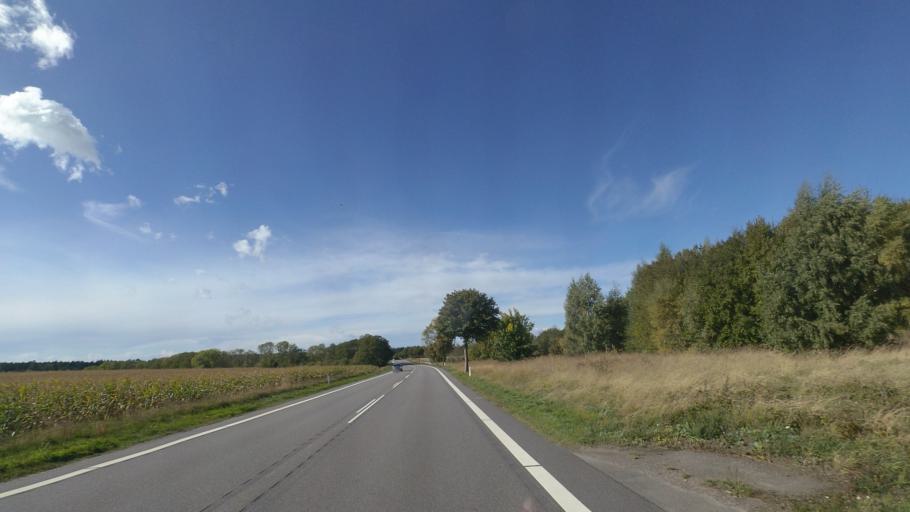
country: DK
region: Capital Region
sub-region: Bornholm Kommune
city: Ronne
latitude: 55.0776
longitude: 14.7693
